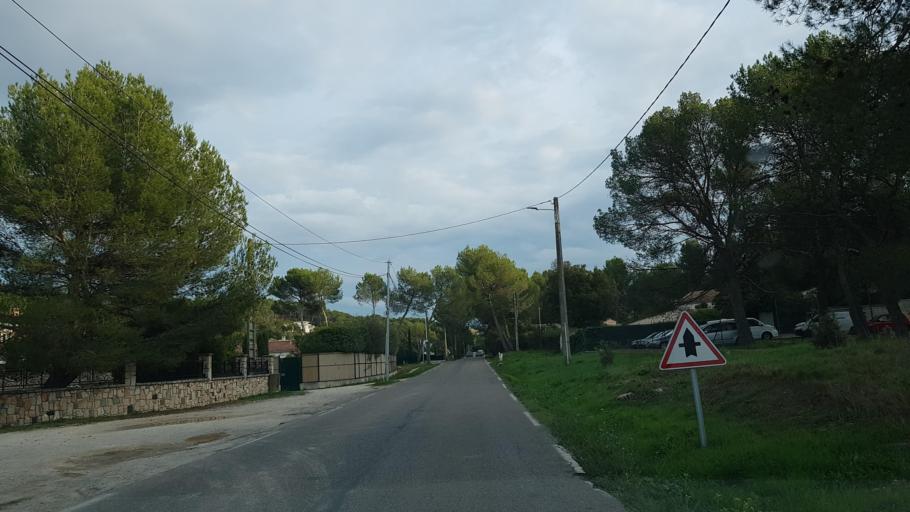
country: FR
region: Provence-Alpes-Cote d'Azur
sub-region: Departement des Bouches-du-Rhone
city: Cabries
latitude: 43.4523
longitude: 5.3593
